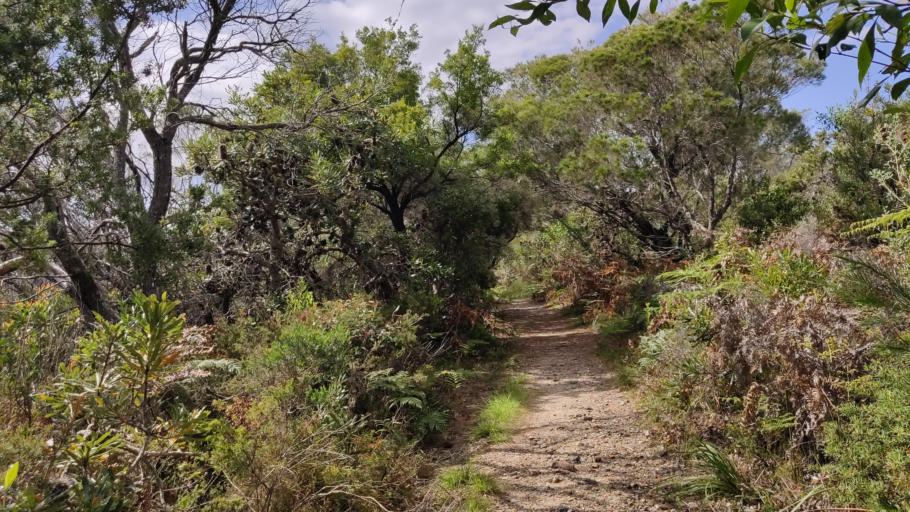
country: AU
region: New South Wales
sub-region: Port Macquarie-Hastings
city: North Haven
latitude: -31.6441
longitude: 152.8367
